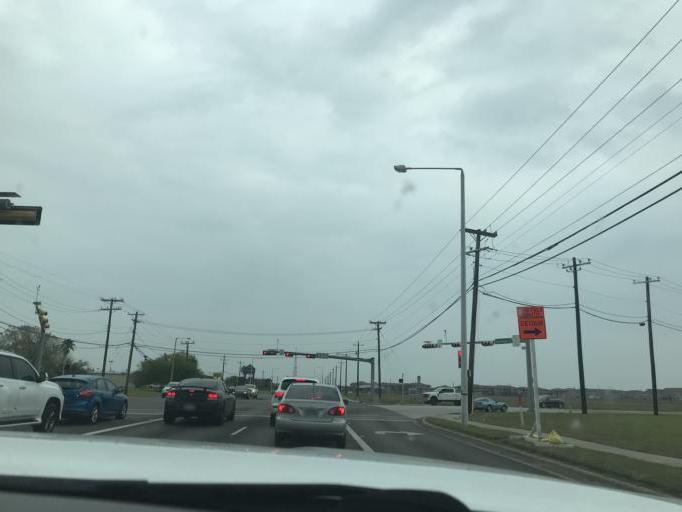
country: US
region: Texas
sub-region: Nueces County
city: Corpus Christi
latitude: 27.6759
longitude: -97.3647
